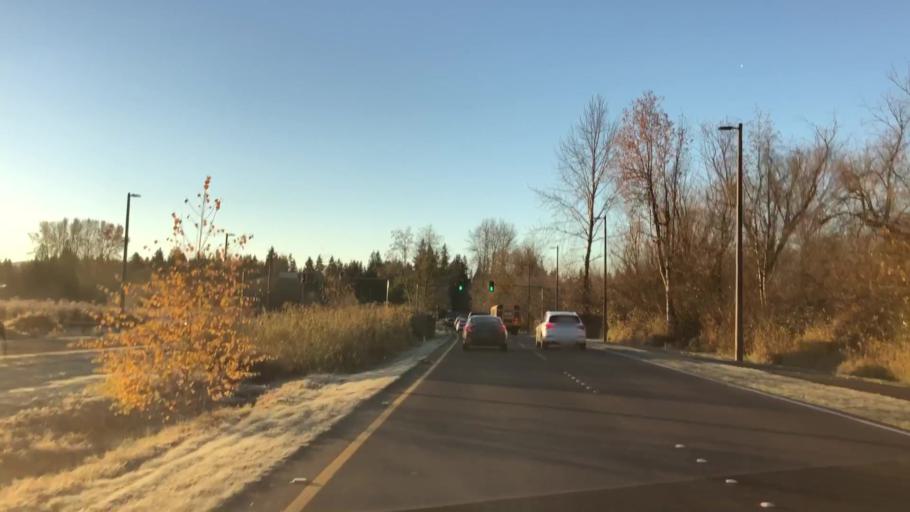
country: US
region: Washington
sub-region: King County
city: Eastgate
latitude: 47.6065
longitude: -122.1430
